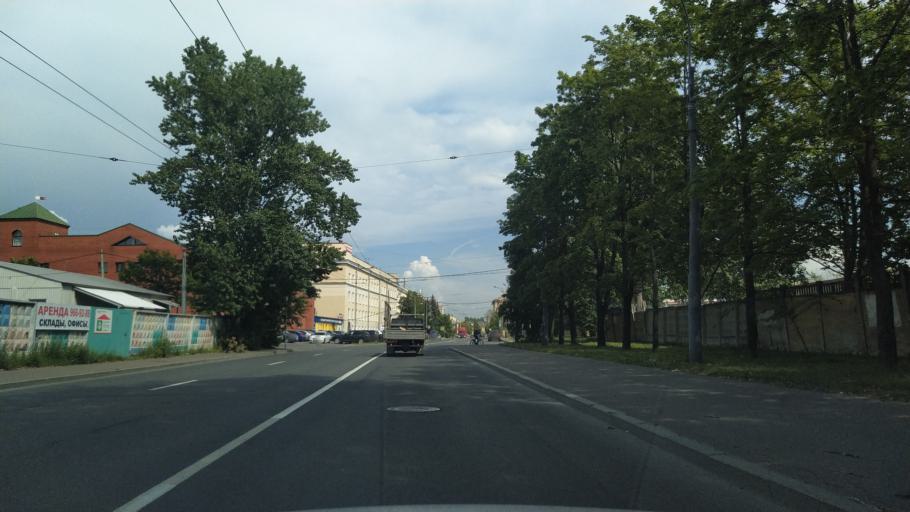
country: RU
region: Leningrad
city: Finlyandskiy
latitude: 59.9654
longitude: 30.3700
